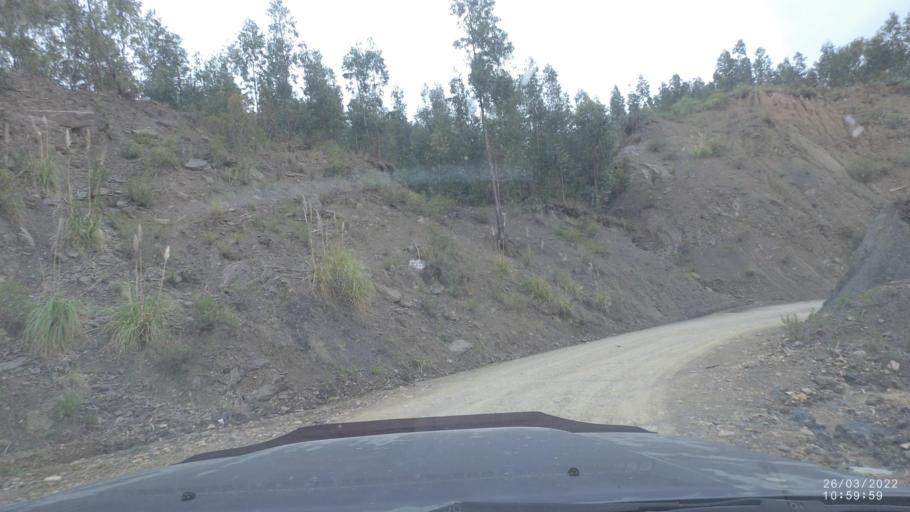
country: BO
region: Cochabamba
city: Tarata
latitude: -17.5139
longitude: -66.0247
